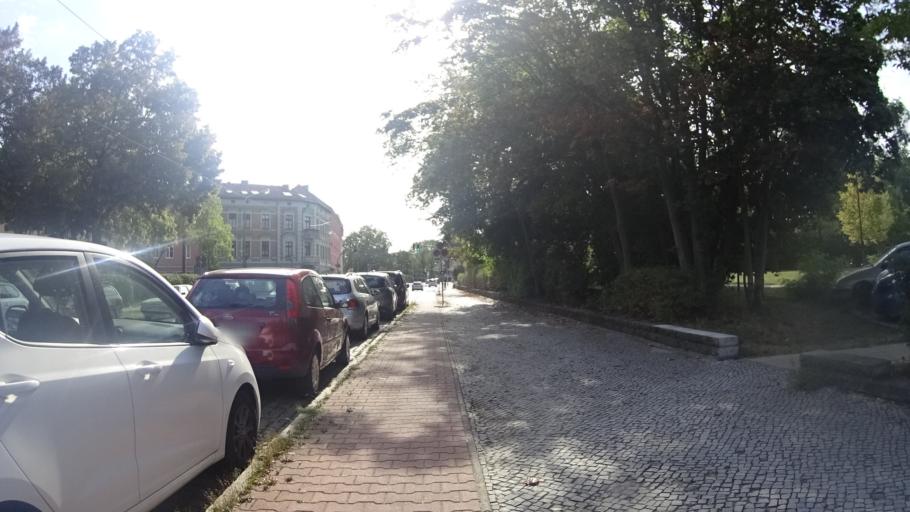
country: DE
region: Brandenburg
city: Brandenburg an der Havel
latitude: 52.4115
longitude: 12.5462
